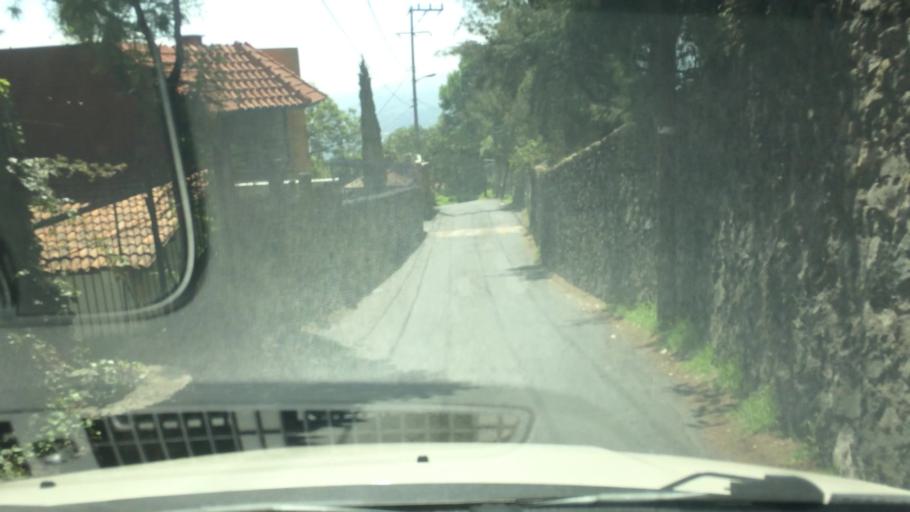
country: MX
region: Mexico City
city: Xochimilco
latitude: 19.2359
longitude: -99.1553
